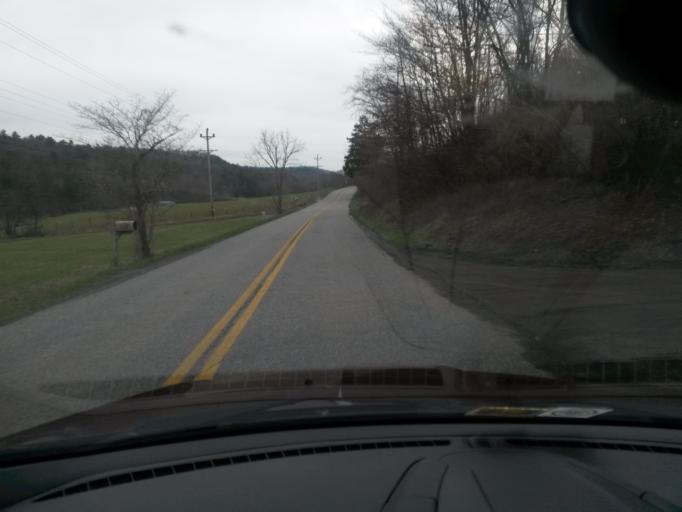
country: US
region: Virginia
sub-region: Bath County
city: Warm Springs
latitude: 37.9969
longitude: -79.8873
